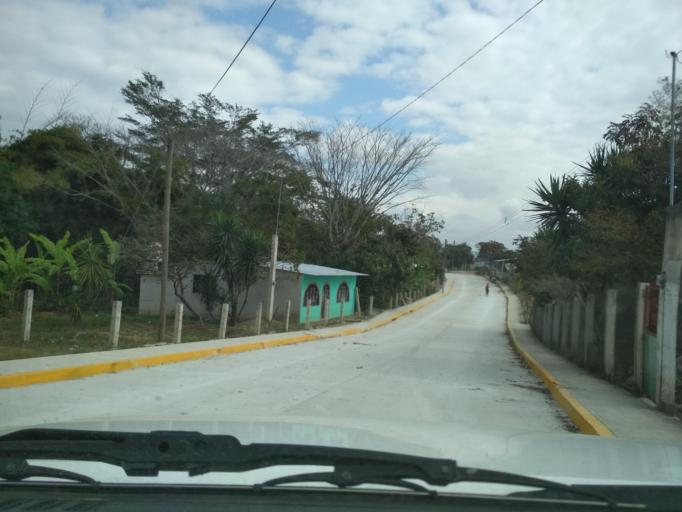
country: MX
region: Veracruz
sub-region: Coatepec
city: Tuzamapan
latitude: 19.3698
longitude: -96.8787
